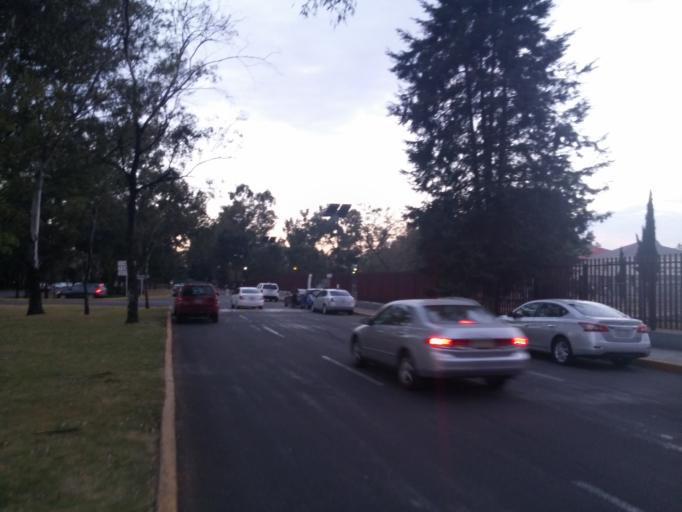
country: MX
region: Mexico
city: Colonia Lindavista
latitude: 19.4998
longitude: -99.1401
